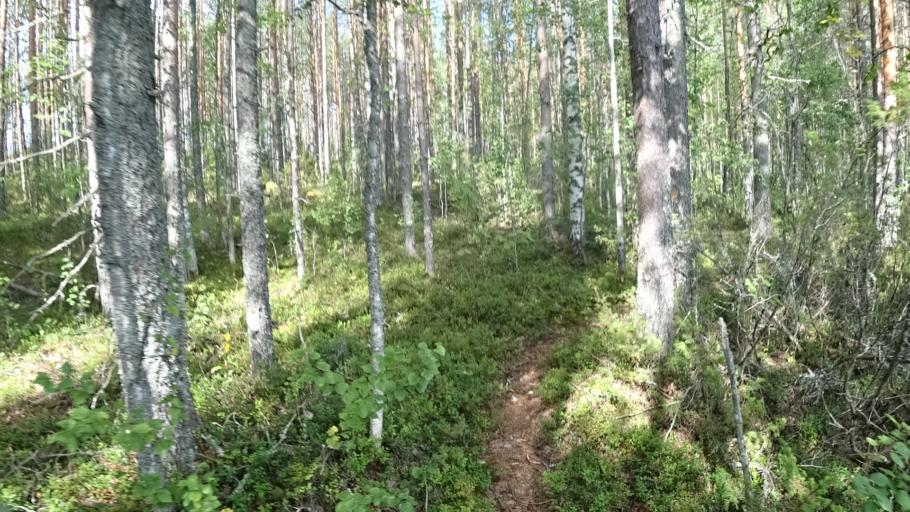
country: FI
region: North Karelia
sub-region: Joensuu
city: Ilomantsi
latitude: 62.6110
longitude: 31.1887
